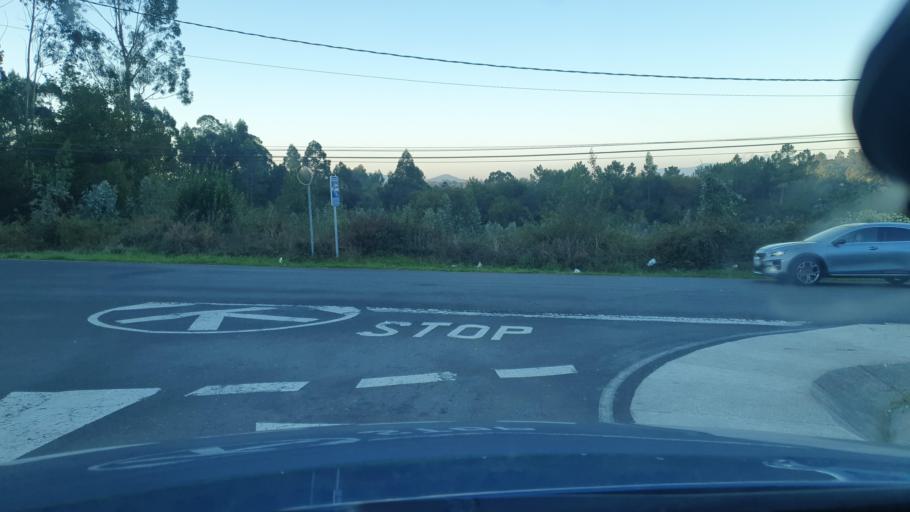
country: ES
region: Galicia
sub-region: Provincia da Coruna
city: Santiago de Compostela
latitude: 42.8444
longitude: -8.5842
